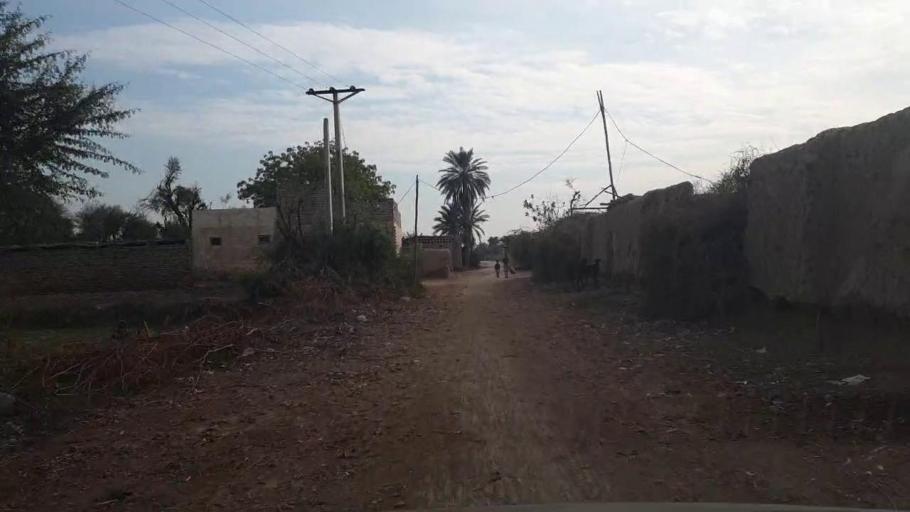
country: PK
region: Sindh
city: Shahdadpur
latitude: 26.0460
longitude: 68.5765
